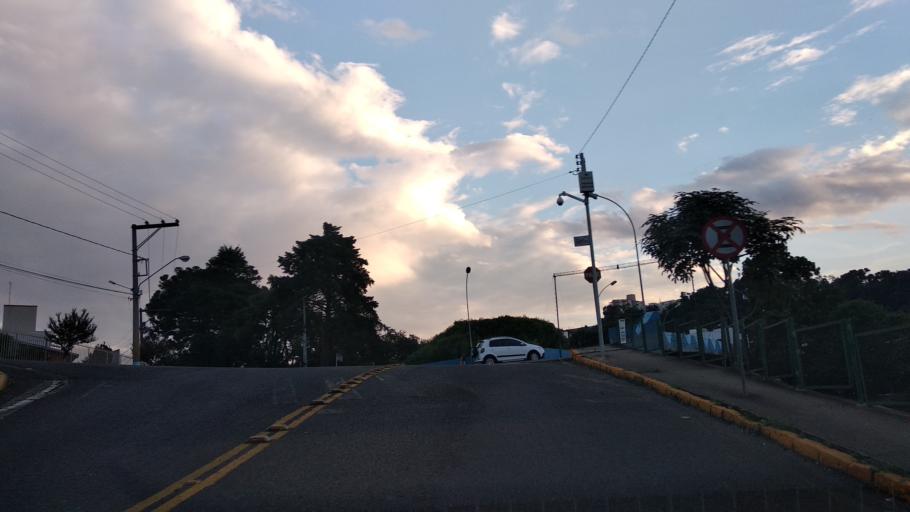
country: BR
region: Santa Catarina
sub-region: Videira
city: Videira
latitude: -27.0007
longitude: -51.1568
